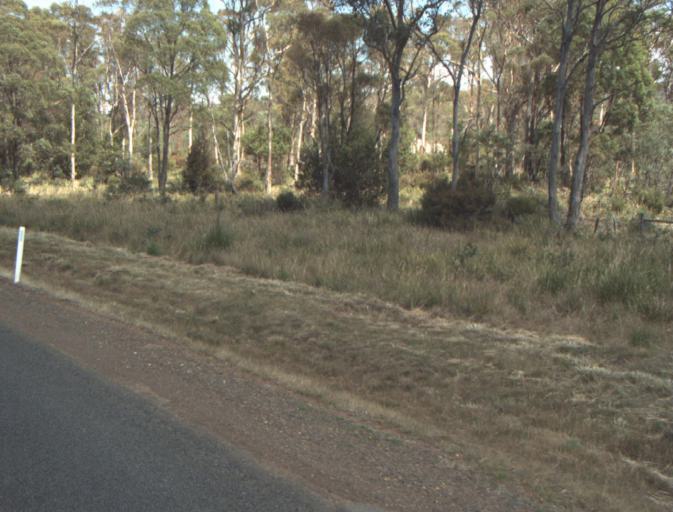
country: AU
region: Tasmania
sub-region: Launceston
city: Mayfield
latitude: -41.3239
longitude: 147.1372
